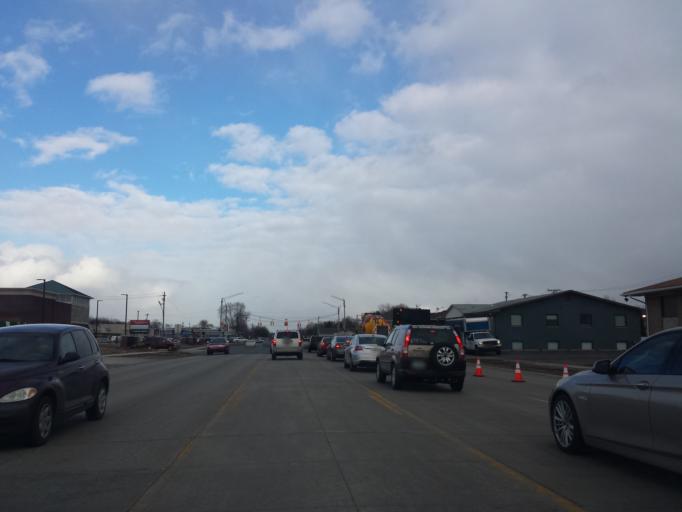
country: US
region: Michigan
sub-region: Oakland County
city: Lathrup Village
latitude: 42.5024
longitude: -83.2249
